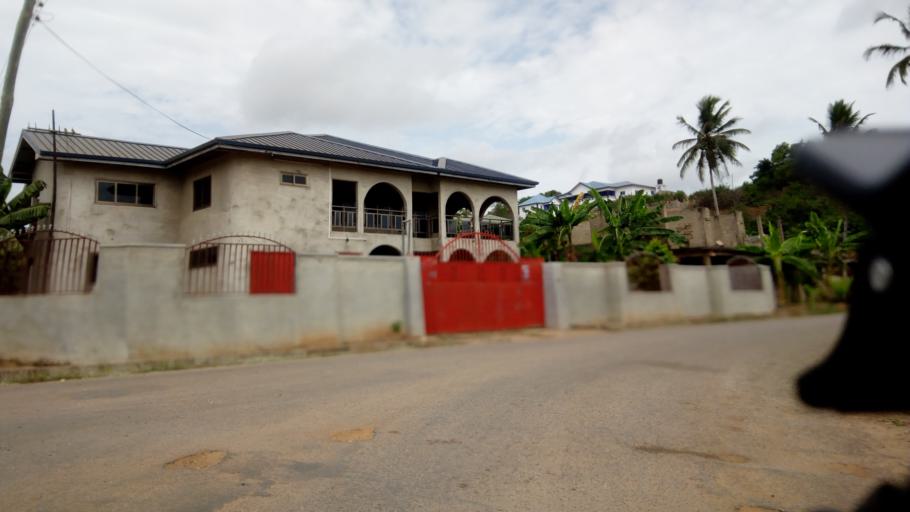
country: GH
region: Central
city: Cape Coast
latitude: 5.1078
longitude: -1.2722
